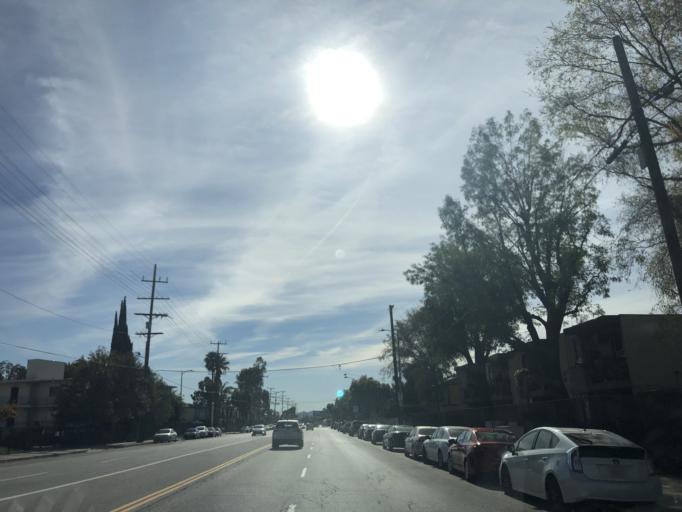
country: US
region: California
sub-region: Los Angeles County
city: North Hollywood
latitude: 34.2277
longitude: -118.3662
